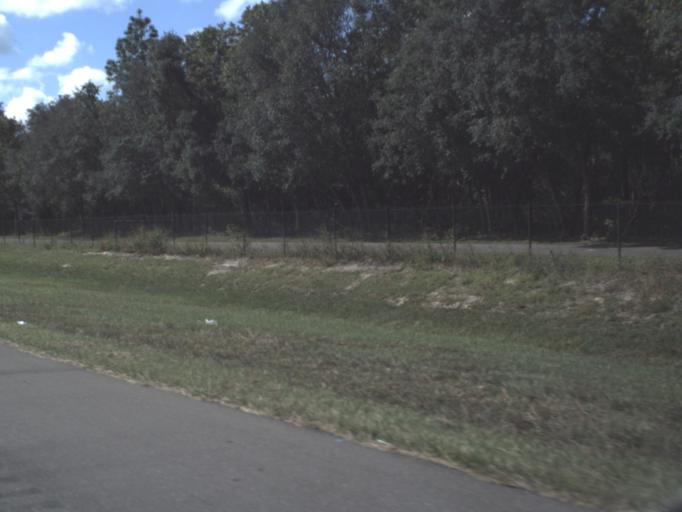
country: US
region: Florida
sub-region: Hernando County
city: Masaryktown
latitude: 28.4612
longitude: -82.4788
